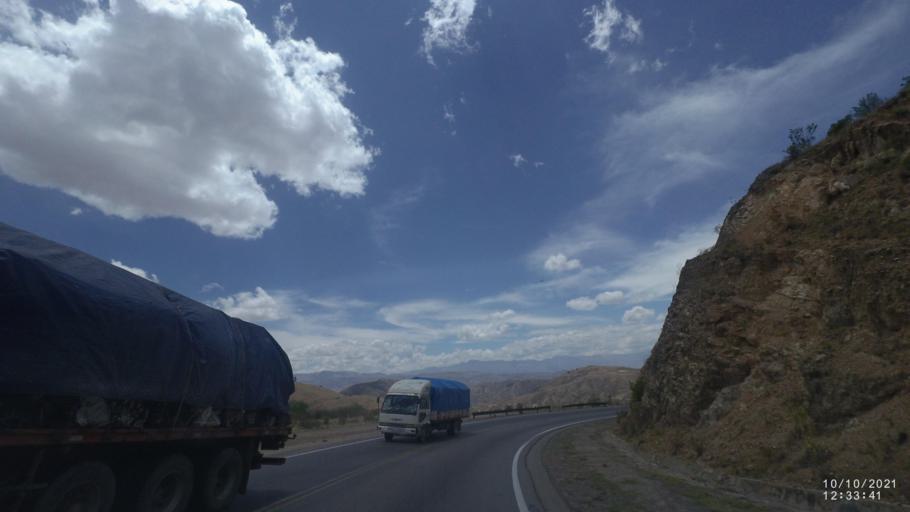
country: BO
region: Cochabamba
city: Irpa Irpa
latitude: -17.6610
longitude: -66.4287
